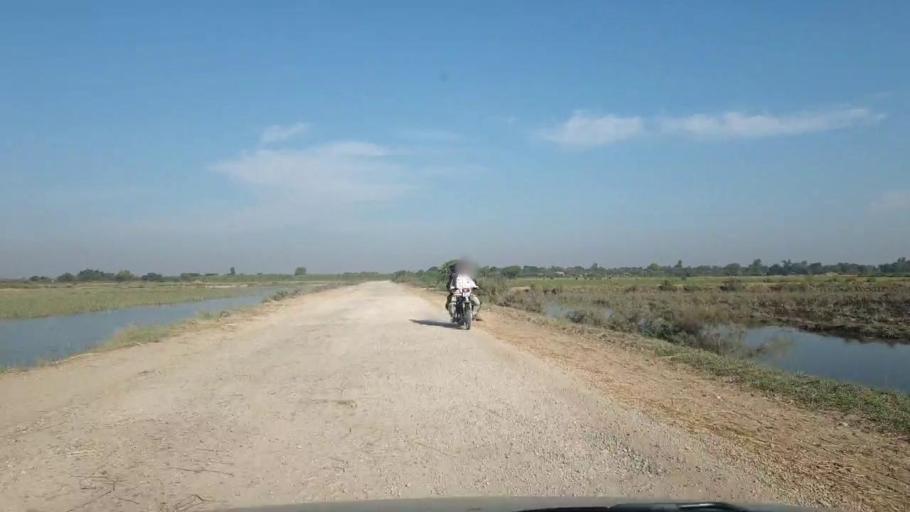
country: PK
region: Sindh
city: Talhar
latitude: 24.9201
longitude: 68.8010
